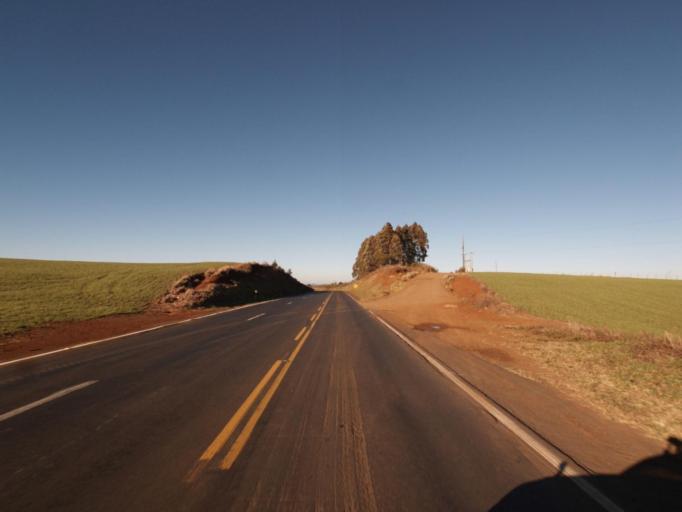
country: AR
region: Misiones
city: Bernardo de Irigoyen
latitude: -26.3183
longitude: -53.5498
